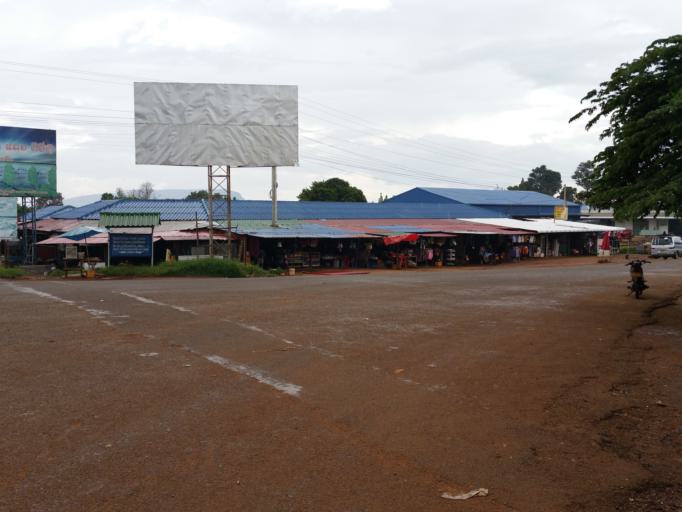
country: LA
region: Champasak
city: Pakxe
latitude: 15.1665
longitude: 105.9751
